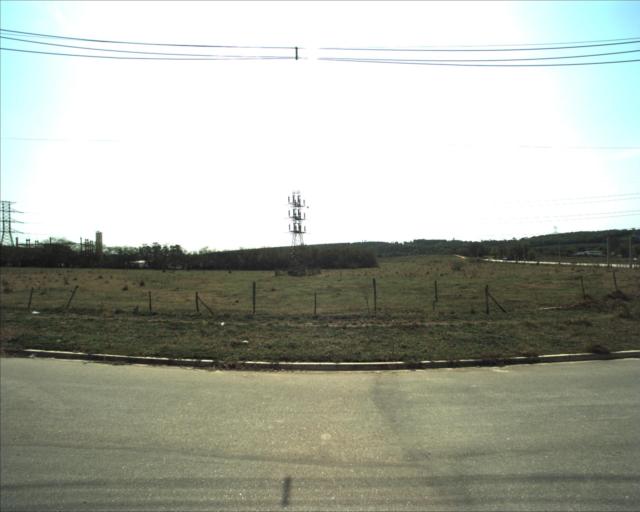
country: BR
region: Sao Paulo
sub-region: Sorocaba
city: Sorocaba
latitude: -23.4225
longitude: -47.4437
